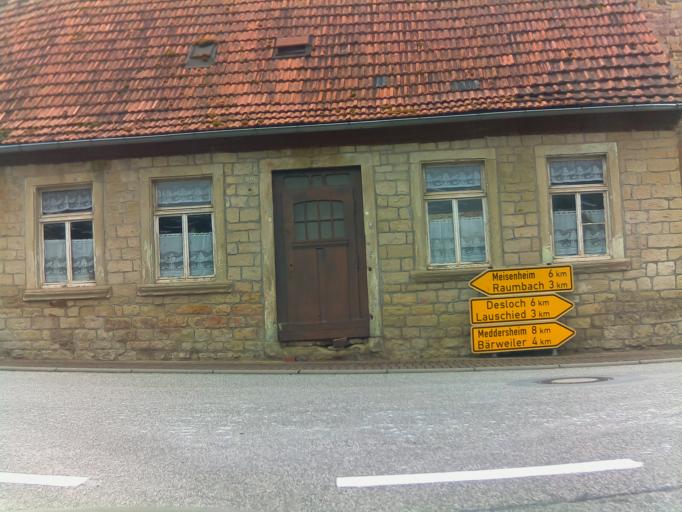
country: DE
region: Rheinland-Pfalz
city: Abtweiler
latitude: 49.7461
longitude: 7.6555
